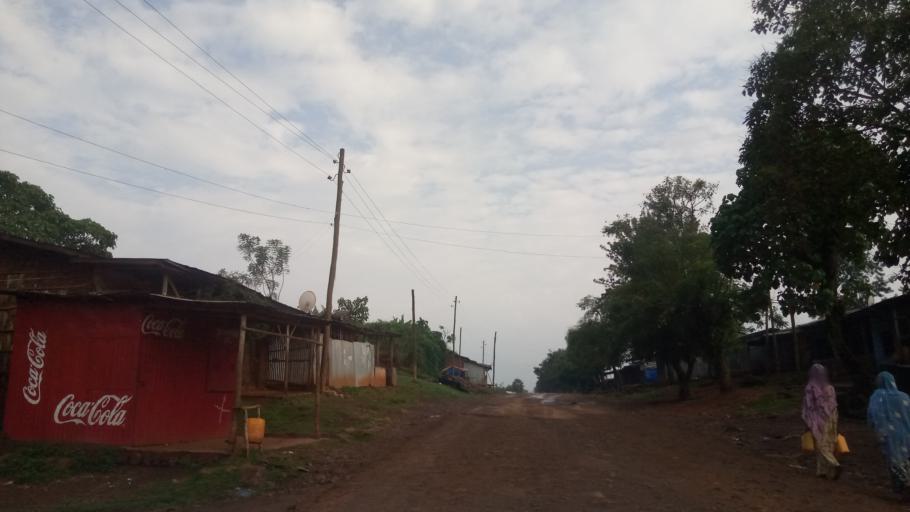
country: ET
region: Oromiya
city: Agaro
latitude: 7.8360
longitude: 36.6719
